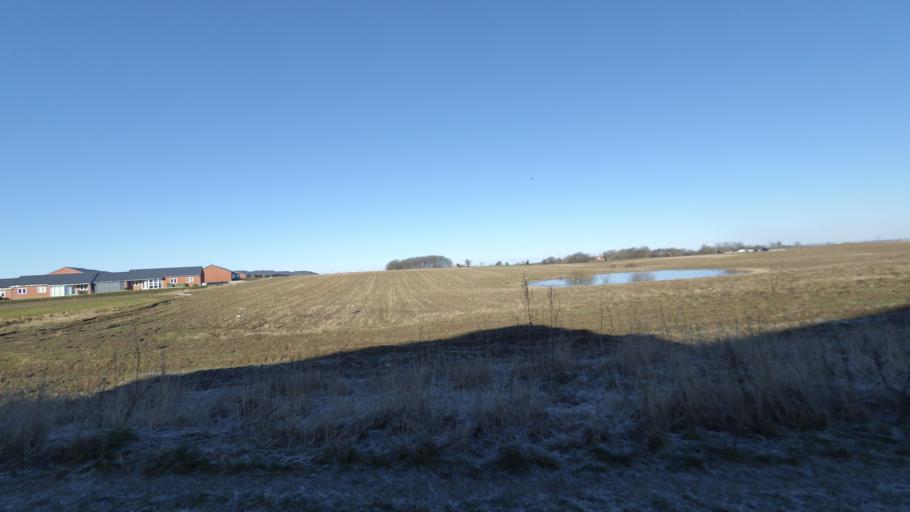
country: DK
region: Central Jutland
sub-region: Arhus Kommune
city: Kolt
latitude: 56.1139
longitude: 10.0923
